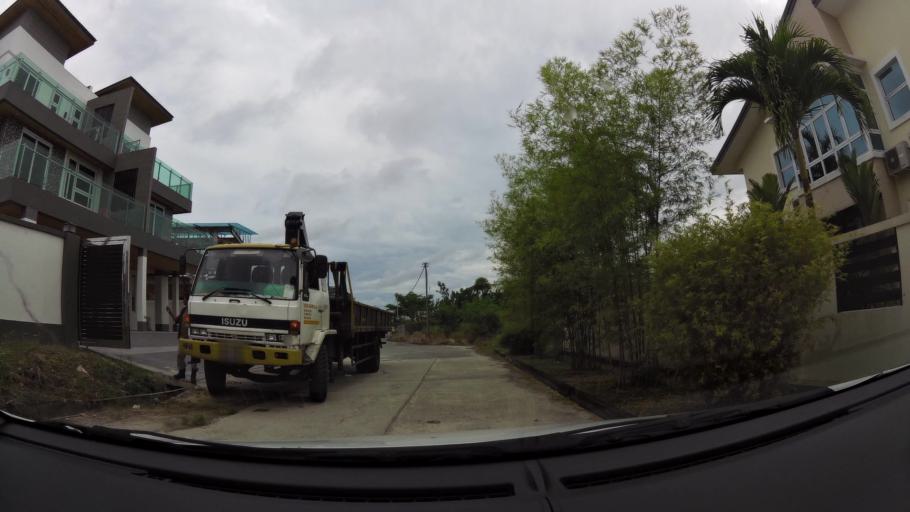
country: BN
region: Brunei and Muara
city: Bandar Seri Begawan
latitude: 4.8888
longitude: 114.9132
